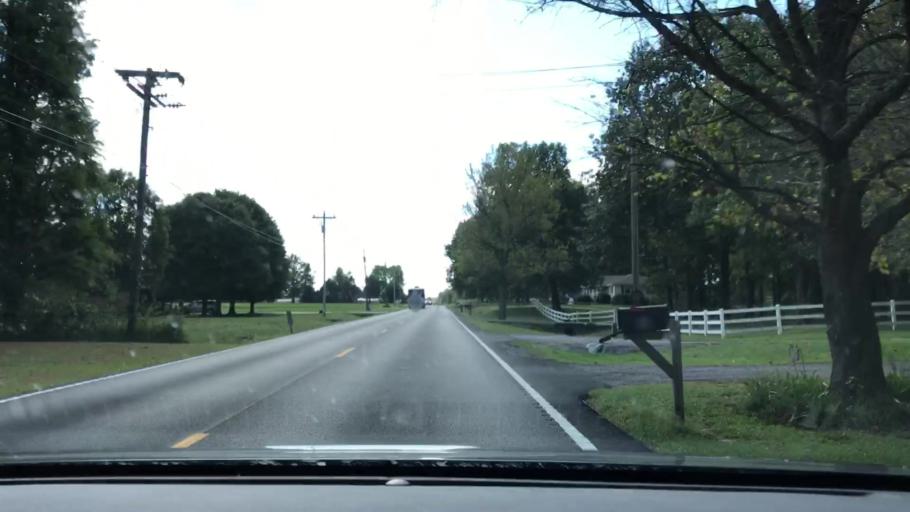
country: US
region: Kentucky
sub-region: Graves County
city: Mayfield
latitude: 36.7682
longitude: -88.5960
